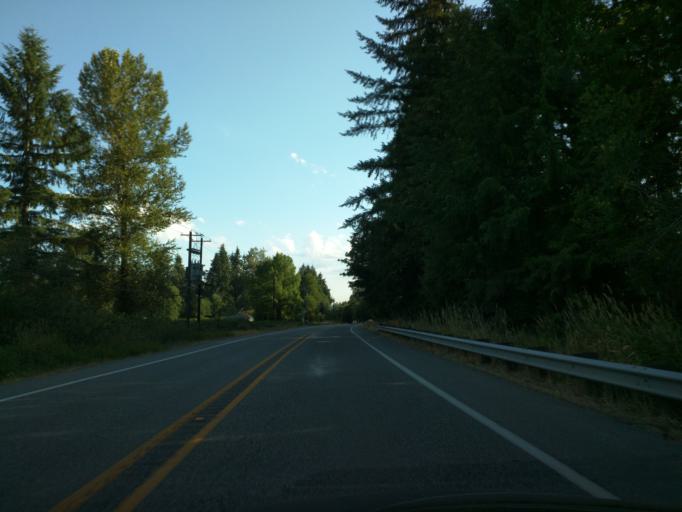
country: US
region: Washington
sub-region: Snohomish County
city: Arlington
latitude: 48.2181
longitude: -122.1083
